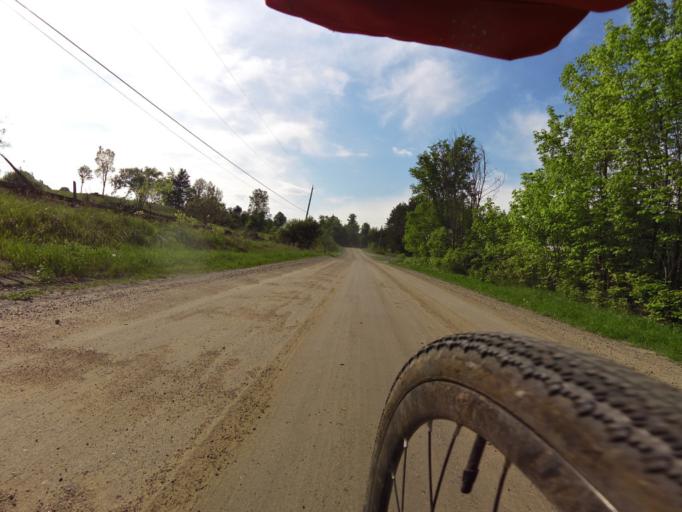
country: CA
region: Ontario
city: Arnprior
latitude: 45.1755
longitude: -76.4717
